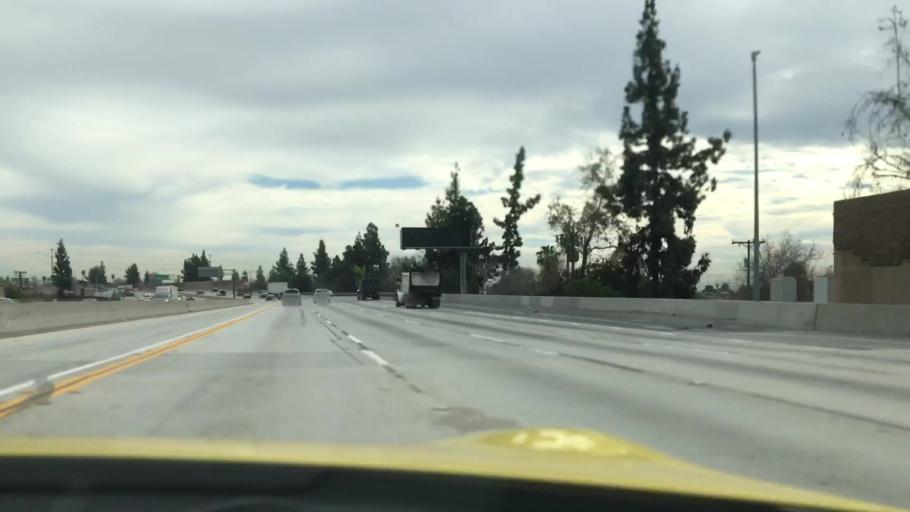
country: US
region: California
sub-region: Los Angeles County
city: Monrovia
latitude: 34.1361
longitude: -118.0096
